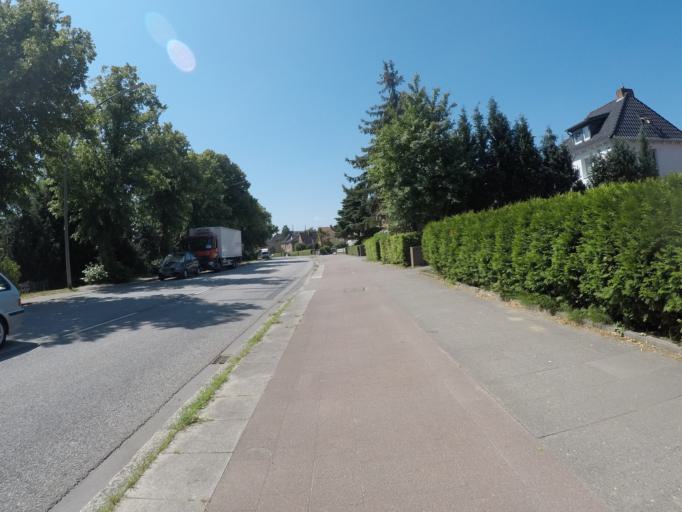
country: DE
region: Hamburg
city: Kleiner Grasbrook
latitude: 53.4938
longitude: 10.0199
